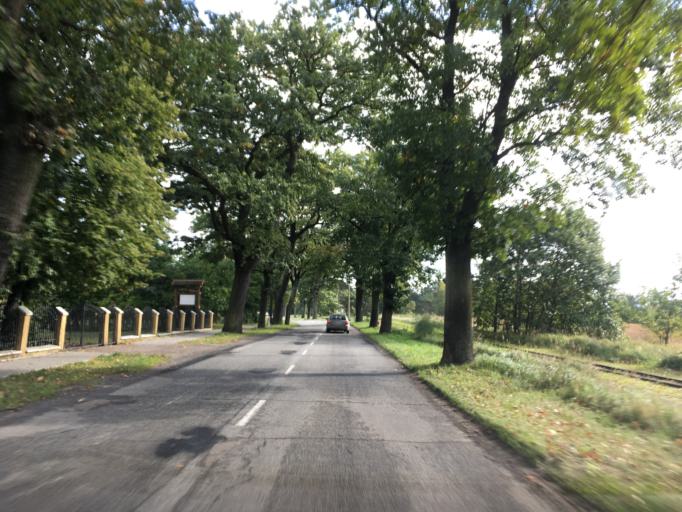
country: PL
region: Pomeranian Voivodeship
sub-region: Powiat nowodworski
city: Ostaszewo
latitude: 54.3330
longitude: 18.9713
